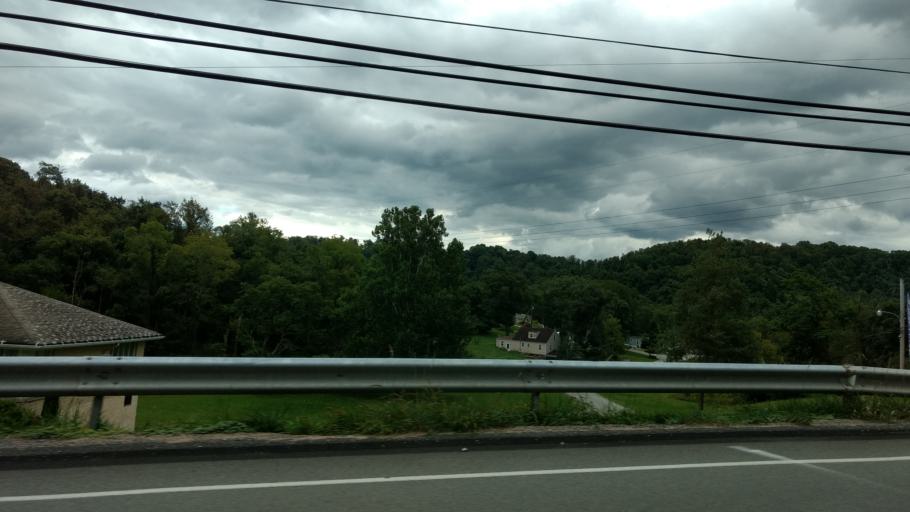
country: US
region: Pennsylvania
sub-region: Westmoreland County
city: Lynnwood-Pricedale
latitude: 40.1503
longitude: -79.8329
